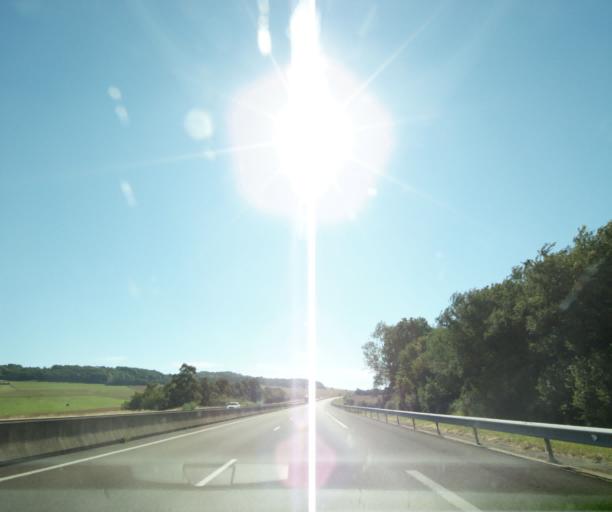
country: FR
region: Champagne-Ardenne
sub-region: Departement de la Haute-Marne
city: Nogent-le-Bas
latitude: 47.9572
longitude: 5.4028
